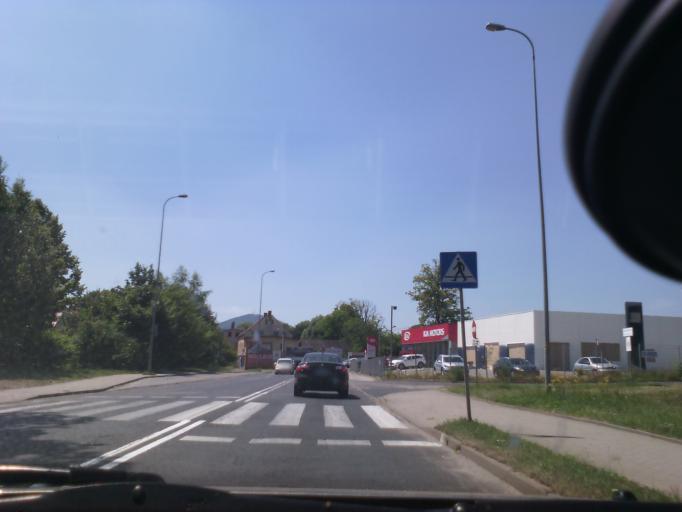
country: PL
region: Lower Silesian Voivodeship
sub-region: Powiat walbrzyski
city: Szczawno-Zdroj
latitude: 50.8136
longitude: 16.2726
